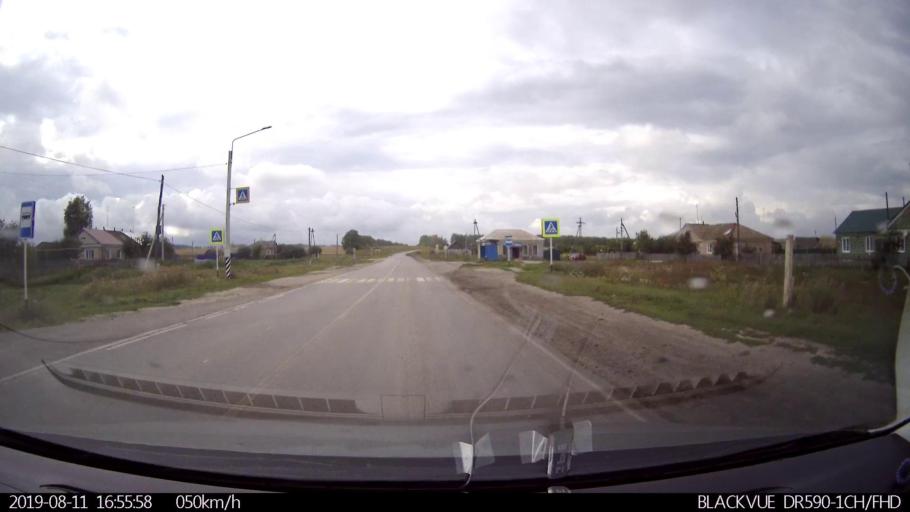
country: RU
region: Ulyanovsk
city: Mayna
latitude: 54.2849
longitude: 47.6583
